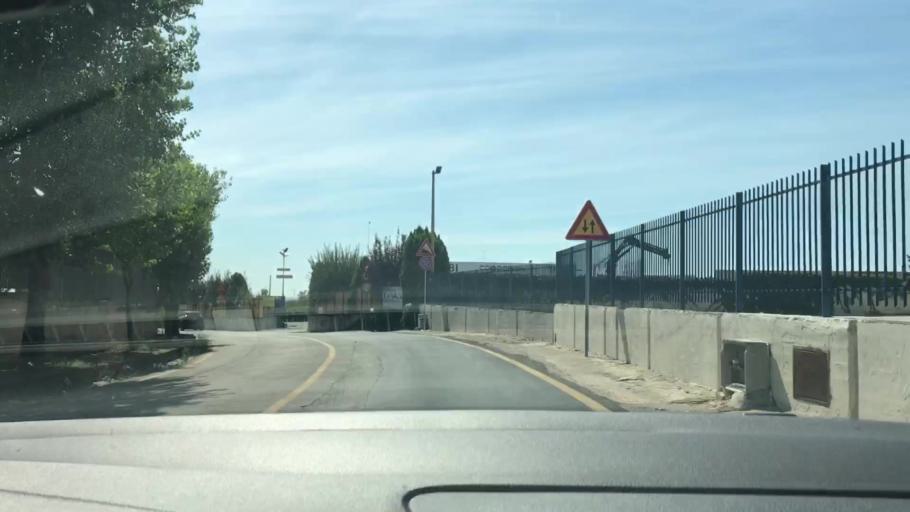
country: IT
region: Apulia
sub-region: Provincia di Bari
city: Altamura
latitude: 40.8120
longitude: 16.5538
